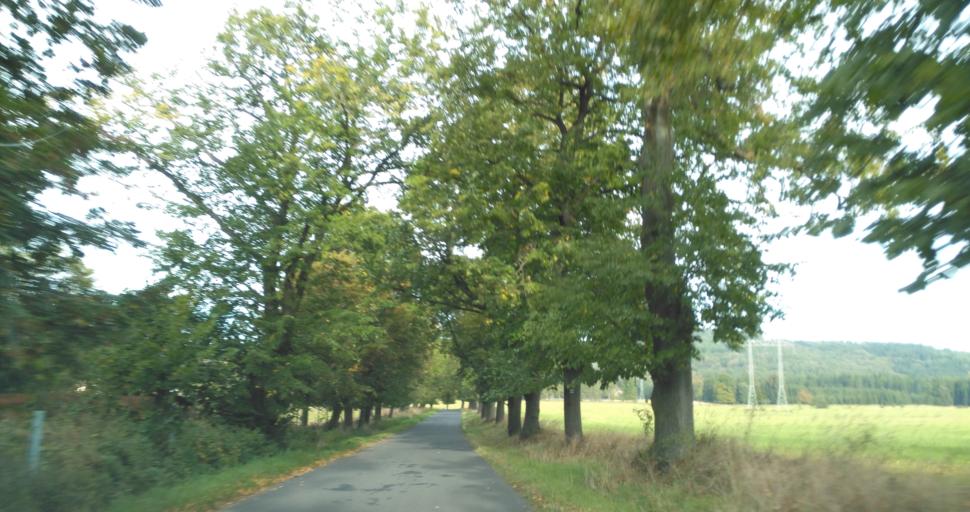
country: CZ
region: Plzensky
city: Zbiroh
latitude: 49.9204
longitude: 13.8182
